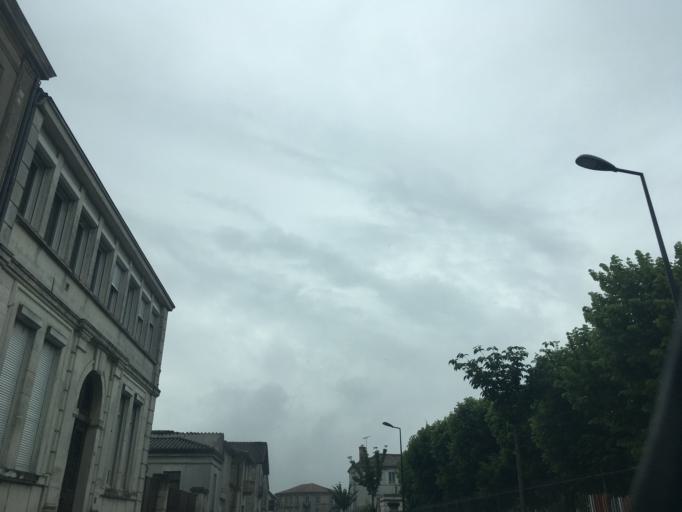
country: FR
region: Poitou-Charentes
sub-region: Departement de la Charente
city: Cognac
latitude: 45.6887
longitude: -0.3275
